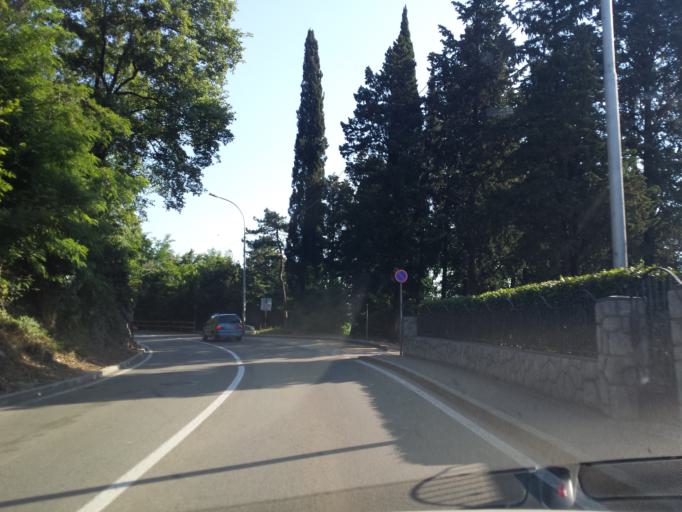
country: HR
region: Primorsko-Goranska
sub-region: Grad Opatija
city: Opatija
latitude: 45.3473
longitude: 14.3161
